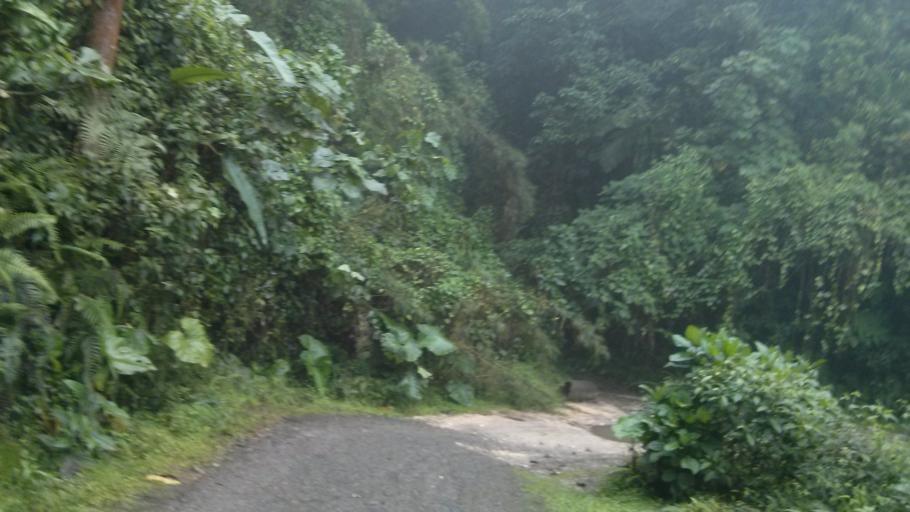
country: CR
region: San Jose
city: Ipis
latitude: 10.0308
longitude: -83.9383
